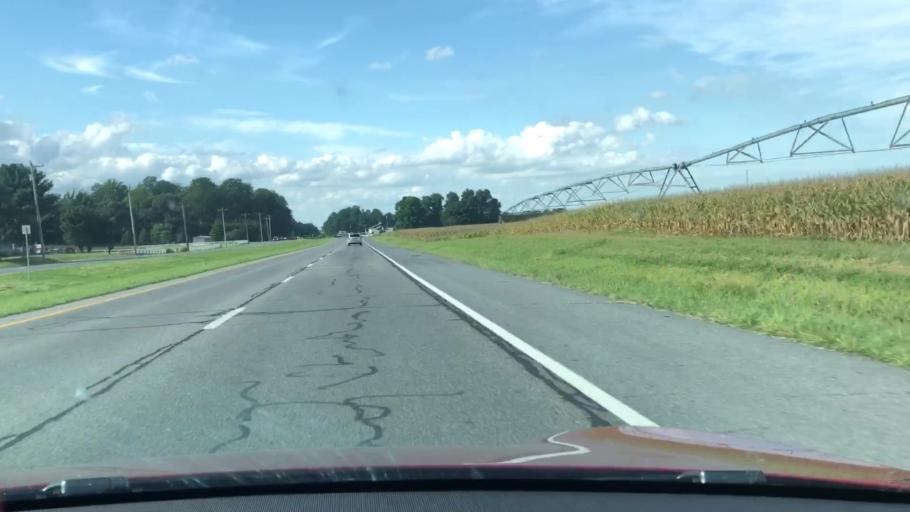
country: US
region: Delaware
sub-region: Kent County
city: Harrington
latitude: 38.9602
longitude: -75.5648
